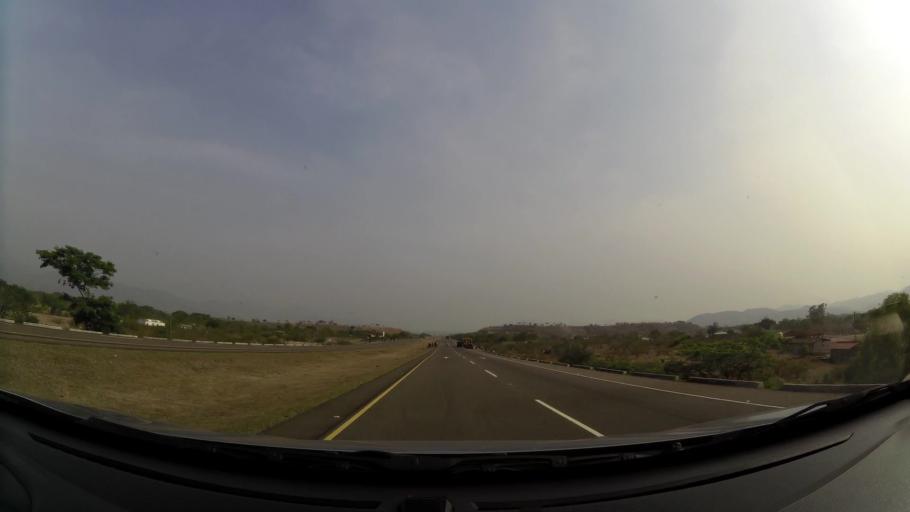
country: HN
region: Comayagua
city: Comayagua
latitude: 14.4429
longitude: -87.6601
